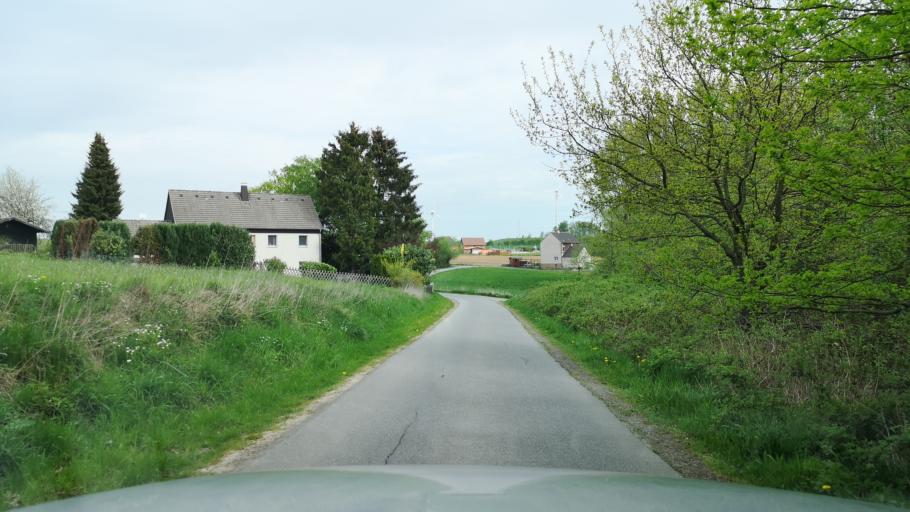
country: DE
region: North Rhine-Westphalia
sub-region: Regierungsbezirk Arnsberg
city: Frondenberg
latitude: 51.4871
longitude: 7.7882
